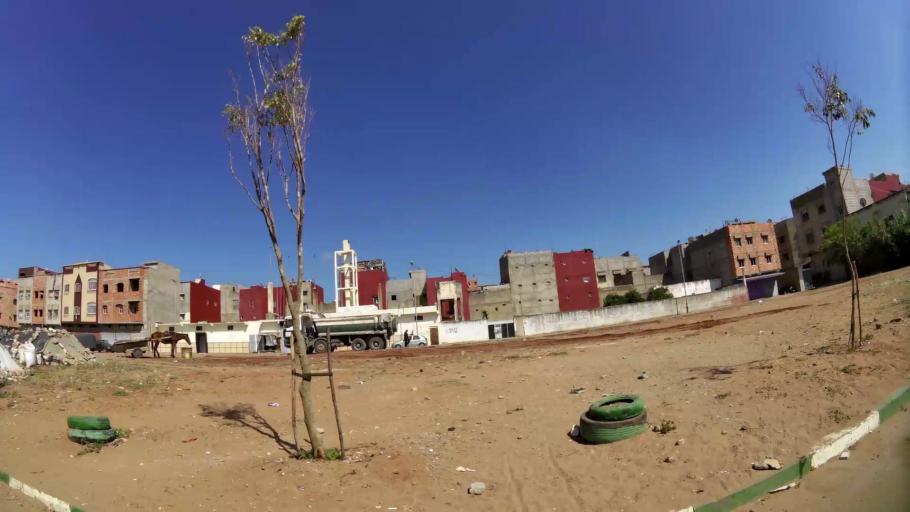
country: MA
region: Rabat-Sale-Zemmour-Zaer
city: Sale
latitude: 34.0692
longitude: -6.7659
